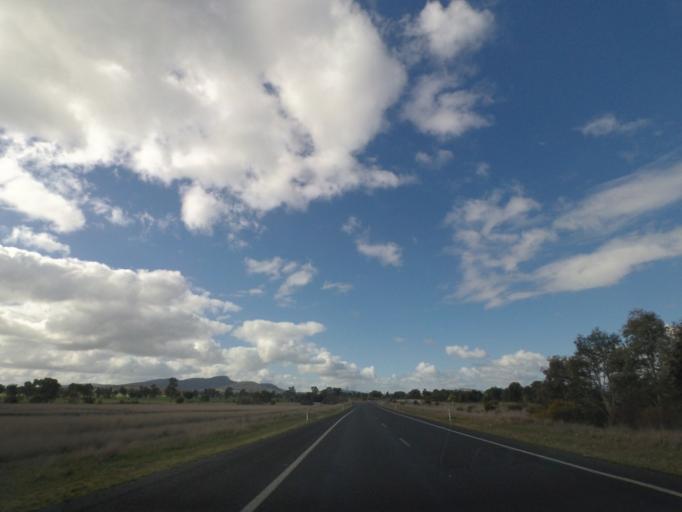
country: AU
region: New South Wales
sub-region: Greater Hume Shire
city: Jindera
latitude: -35.9261
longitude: 147.0072
